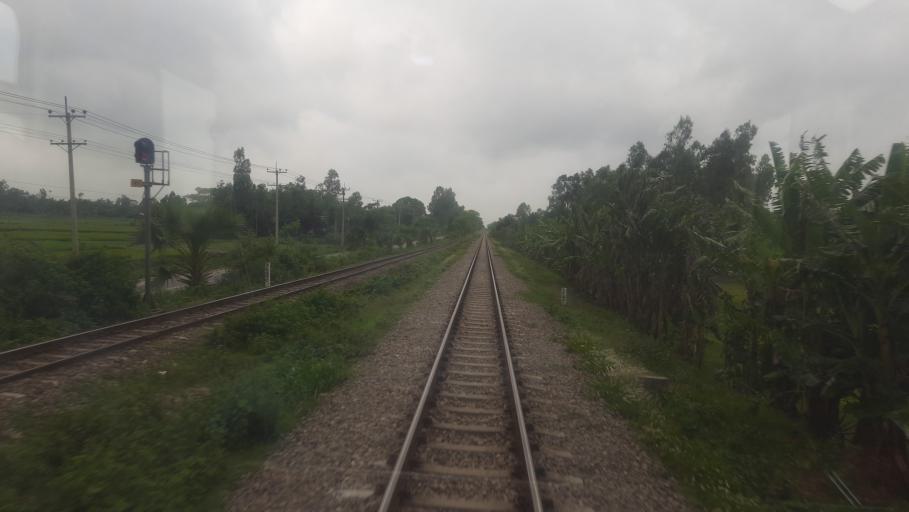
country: BD
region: Dhaka
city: Narsingdi
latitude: 23.9493
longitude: 90.7931
